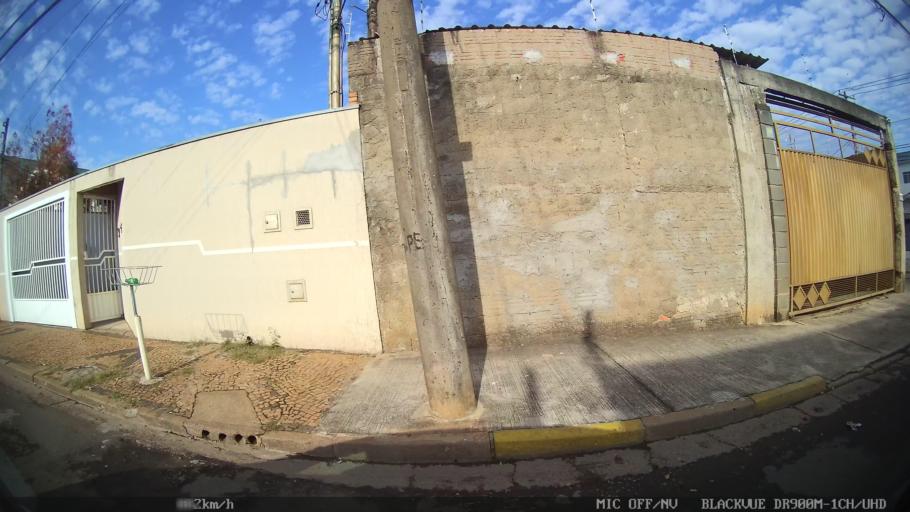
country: BR
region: Sao Paulo
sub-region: Americana
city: Americana
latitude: -22.7368
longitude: -47.3562
